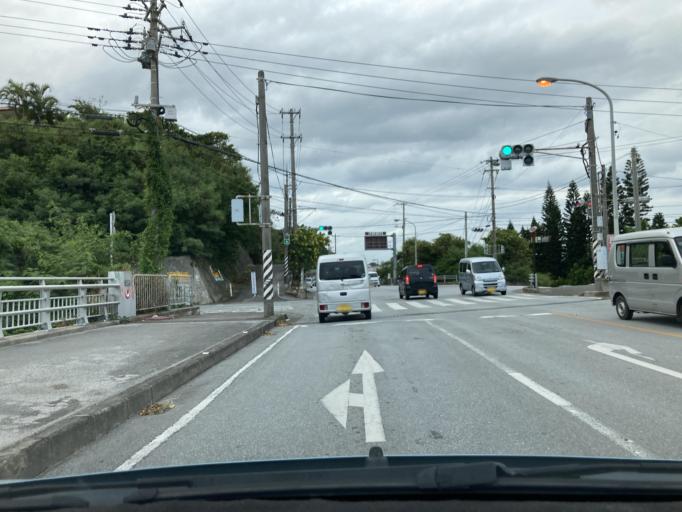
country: JP
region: Okinawa
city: Tomigusuku
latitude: 26.1720
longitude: 127.6910
